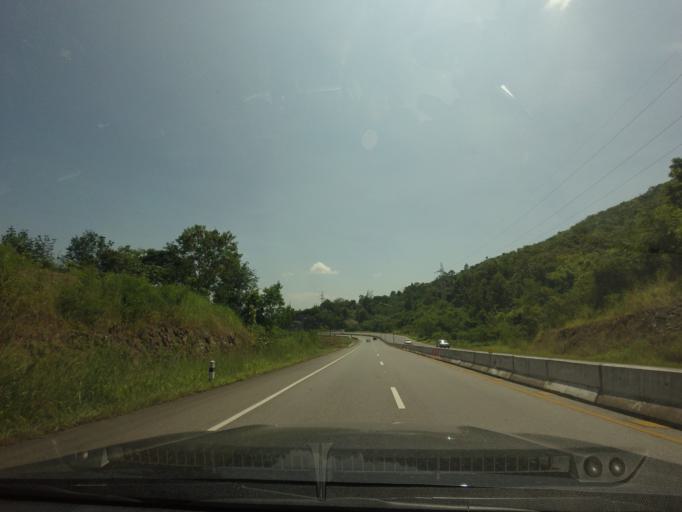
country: TH
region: Phetchabun
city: Lom Sak
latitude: 16.7684
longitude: 101.1372
